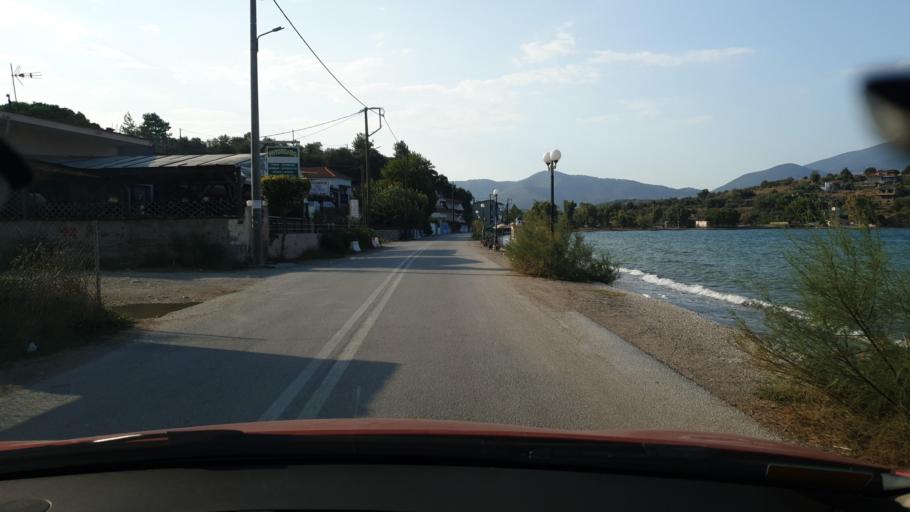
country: GR
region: Thessaly
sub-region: Nomos Magnisias
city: Pteleos
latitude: 39.0074
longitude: 22.9595
